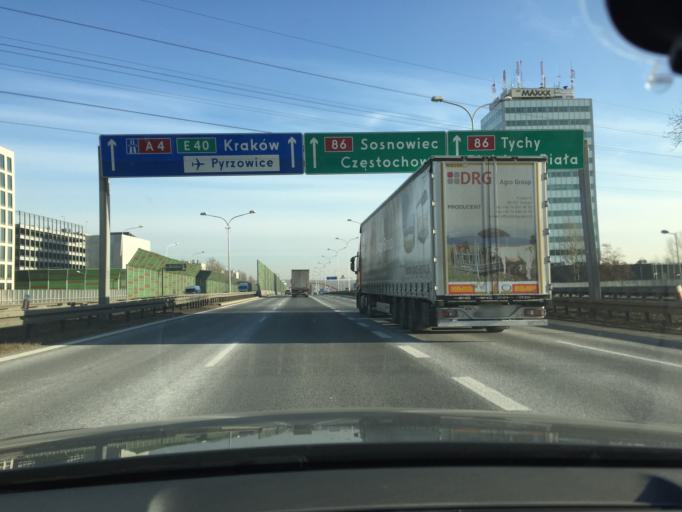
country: PL
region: Silesian Voivodeship
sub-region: Katowice
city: Katowice
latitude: 50.2461
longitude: 19.0248
